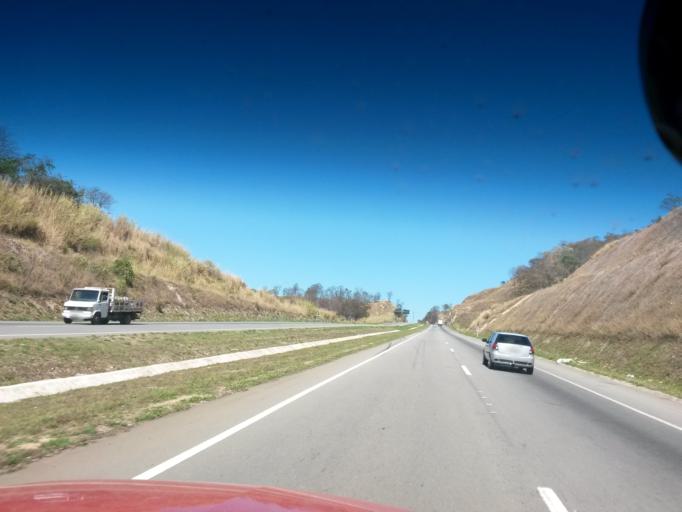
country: BR
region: Minas Gerais
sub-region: Para De Minas
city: Para de Minas
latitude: -19.8906
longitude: -44.6500
